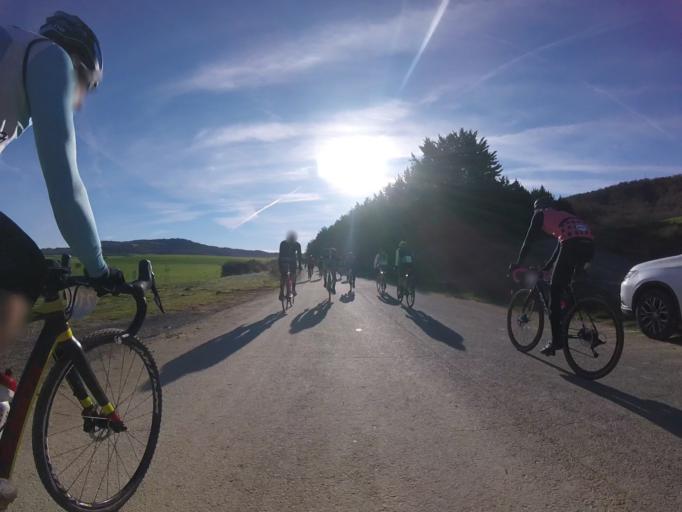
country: ES
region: Navarre
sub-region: Provincia de Navarra
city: Villatuerta
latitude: 42.6558
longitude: -1.9819
